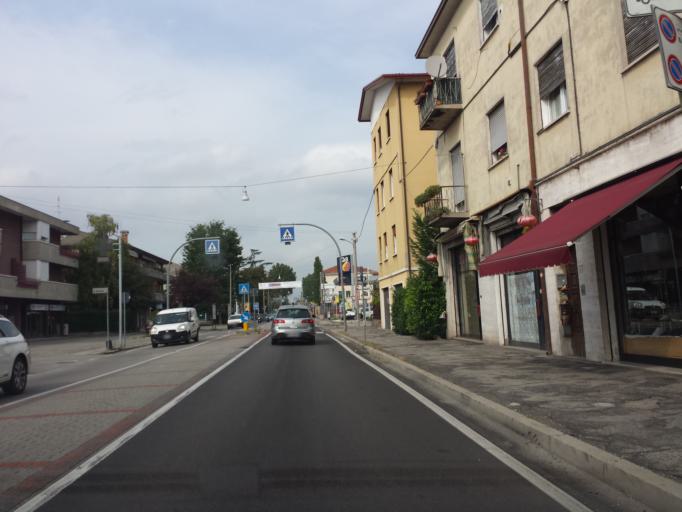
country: IT
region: Veneto
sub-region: Provincia di Padova
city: Vigodarzere
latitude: 45.4426
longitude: 11.8935
